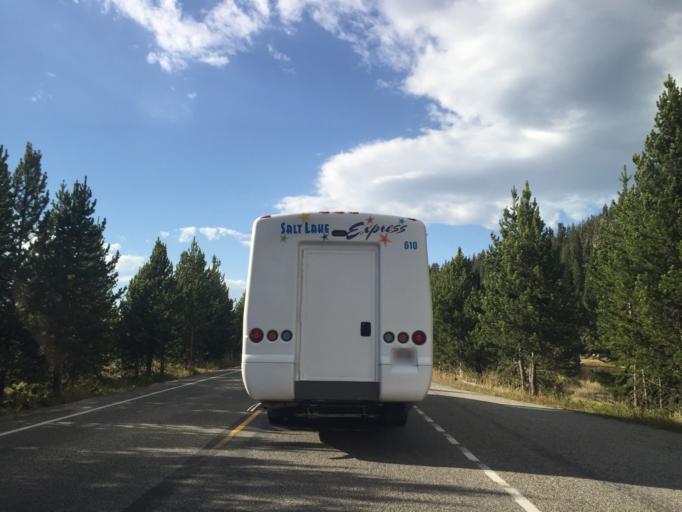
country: US
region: Montana
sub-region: Gallatin County
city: West Yellowstone
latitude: 44.6658
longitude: -110.9689
